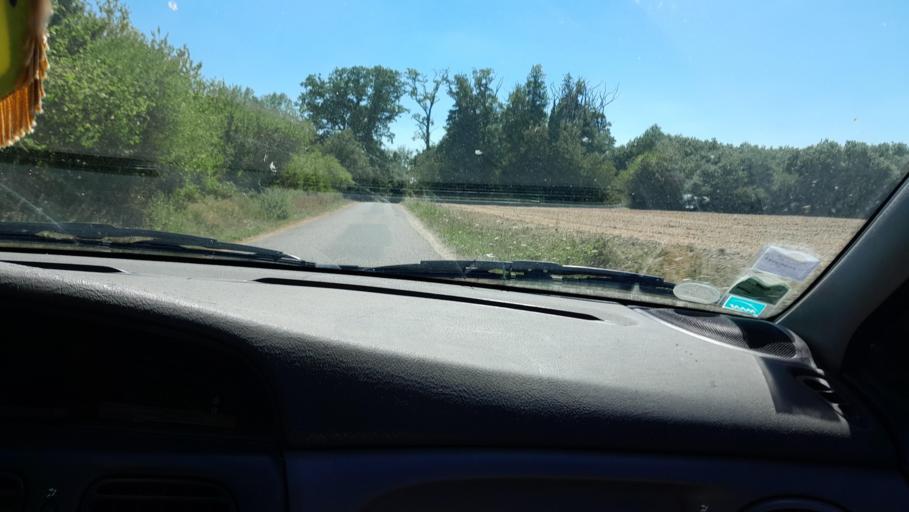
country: FR
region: Pays de la Loire
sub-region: Departement de la Mayenne
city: Congrier
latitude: 47.8229
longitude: -1.1959
